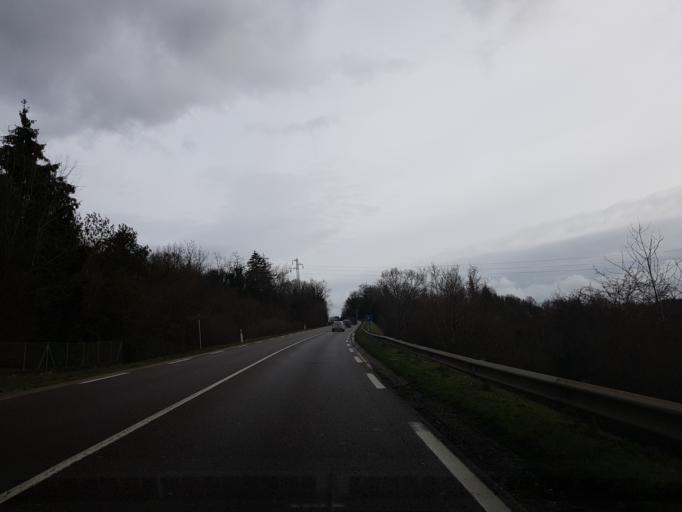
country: FR
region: Franche-Comte
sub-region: Departement de la Haute-Saone
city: Frotey-les-Vesoul
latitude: 47.6263
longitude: 6.1826
